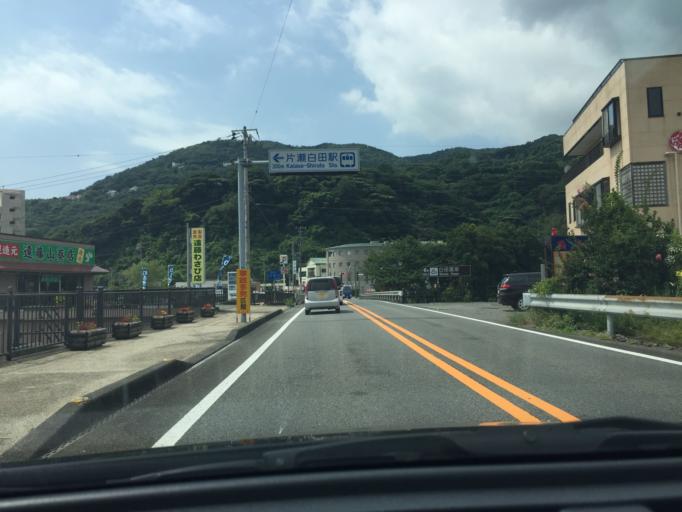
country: JP
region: Shizuoka
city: Ito
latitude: 34.8054
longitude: 139.0590
